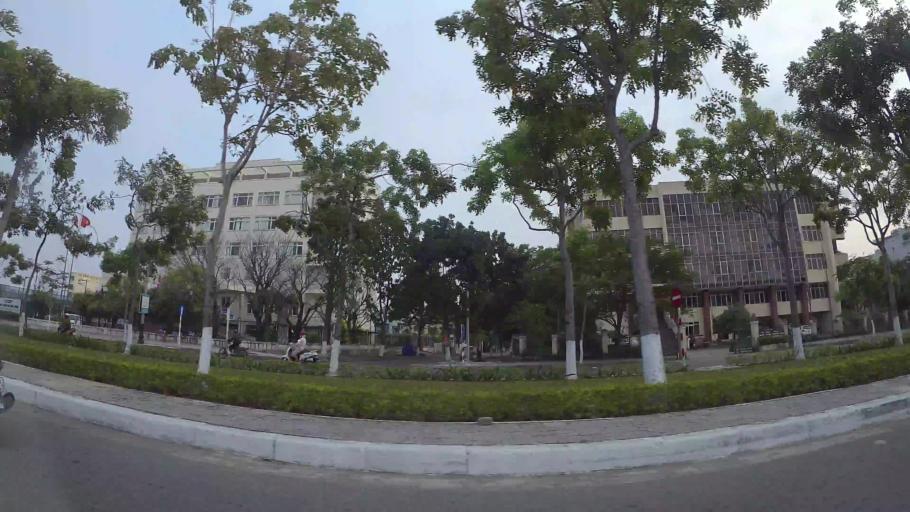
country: VN
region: Da Nang
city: Cam Le
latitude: 16.0334
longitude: 108.2266
